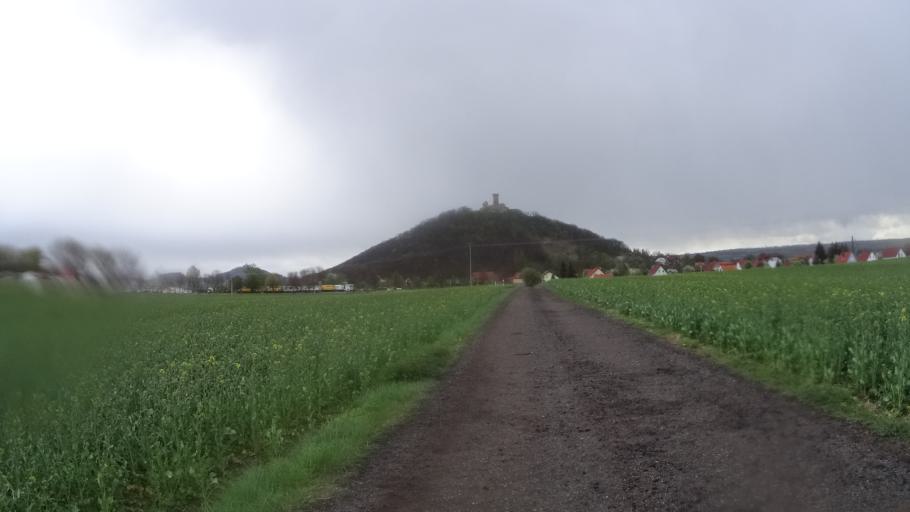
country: DE
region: Thuringia
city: Wandersleben
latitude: 50.8742
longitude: 10.8259
